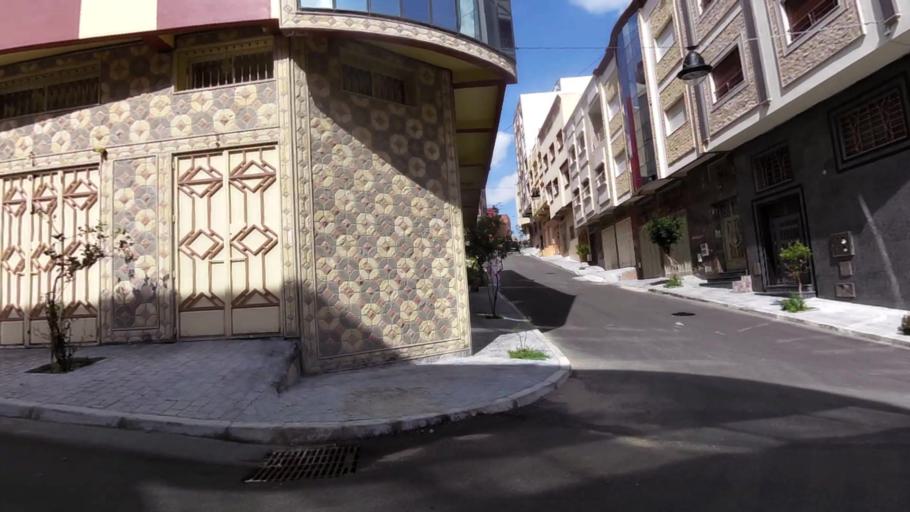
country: MA
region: Tanger-Tetouan
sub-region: Tanger-Assilah
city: Tangier
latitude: 35.7675
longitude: -5.7641
